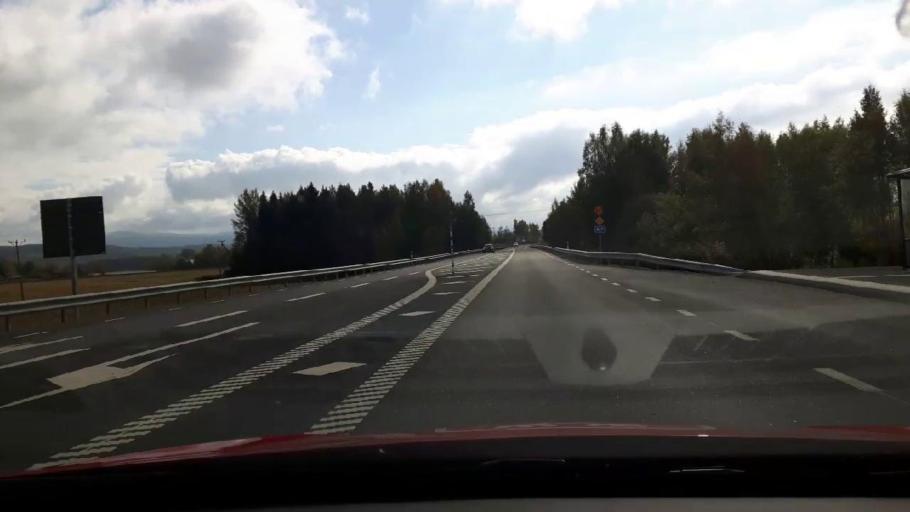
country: SE
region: Gaevleborg
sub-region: Bollnas Kommun
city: Arbra
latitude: 61.5405
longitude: 16.3581
